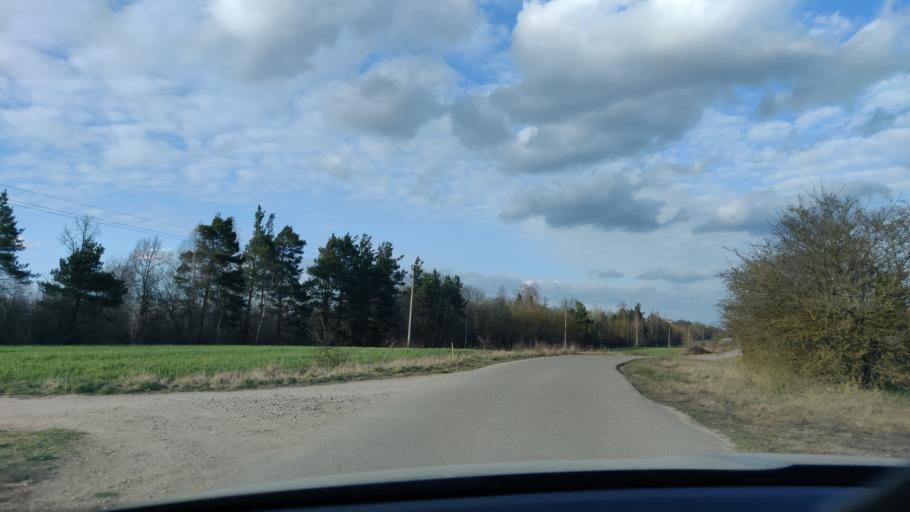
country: LT
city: Trakai
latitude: 54.6068
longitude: 24.9689
